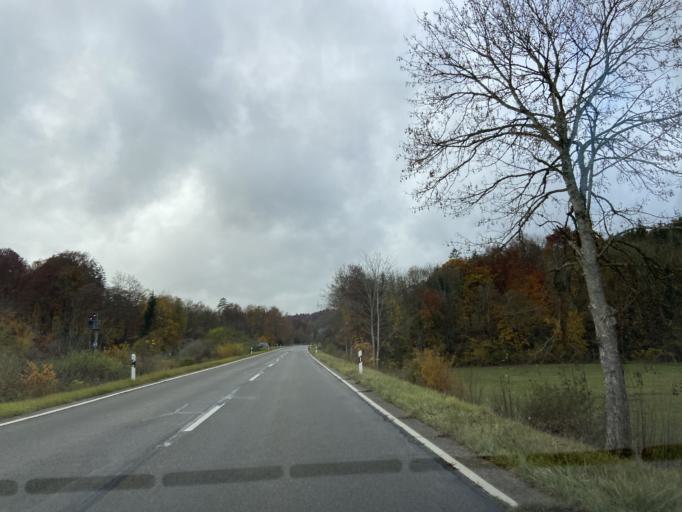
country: DE
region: Baden-Wuerttemberg
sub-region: Tuebingen Region
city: Inzigkofen
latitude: 48.0792
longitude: 9.1806
